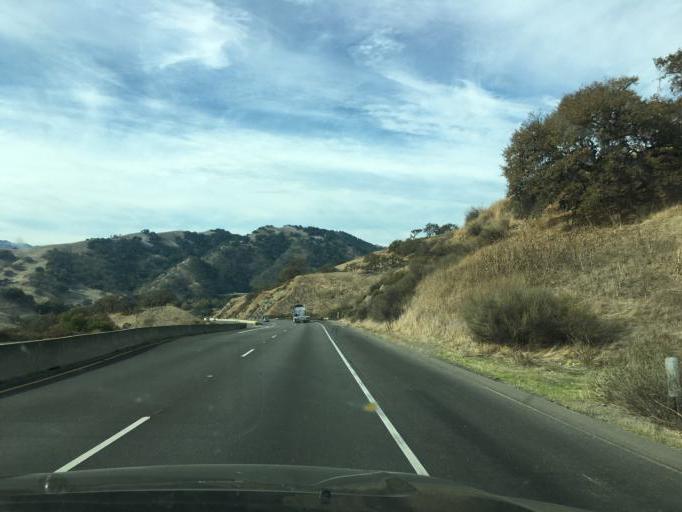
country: US
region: California
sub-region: San Benito County
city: Hollister
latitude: 37.0458
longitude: -121.2746
